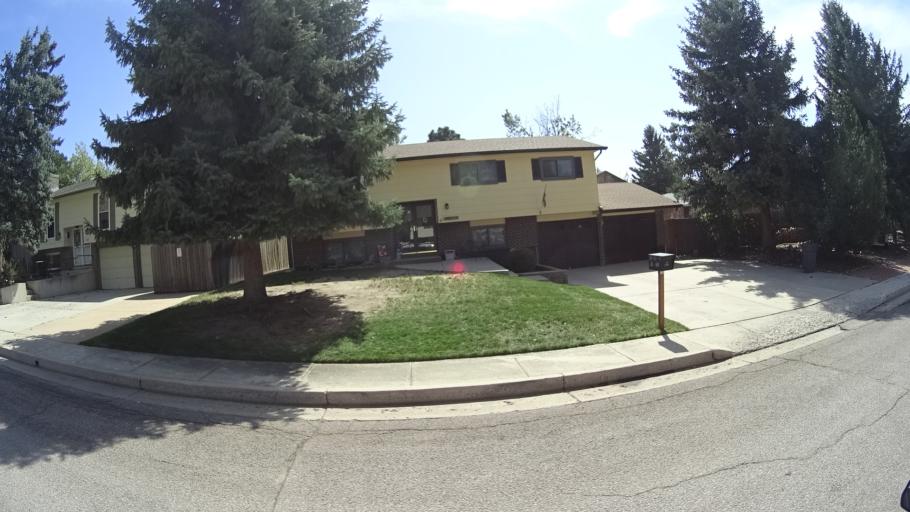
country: US
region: Colorado
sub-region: El Paso County
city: Cimarron Hills
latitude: 38.9134
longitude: -104.7708
